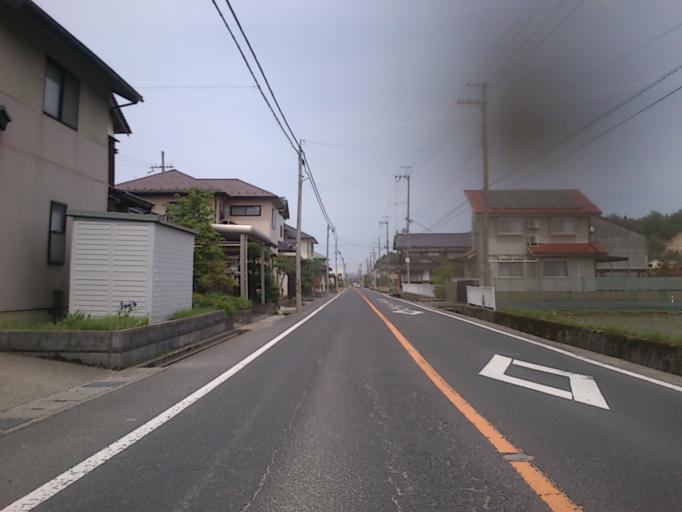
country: JP
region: Kyoto
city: Miyazu
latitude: 35.5920
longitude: 135.0991
